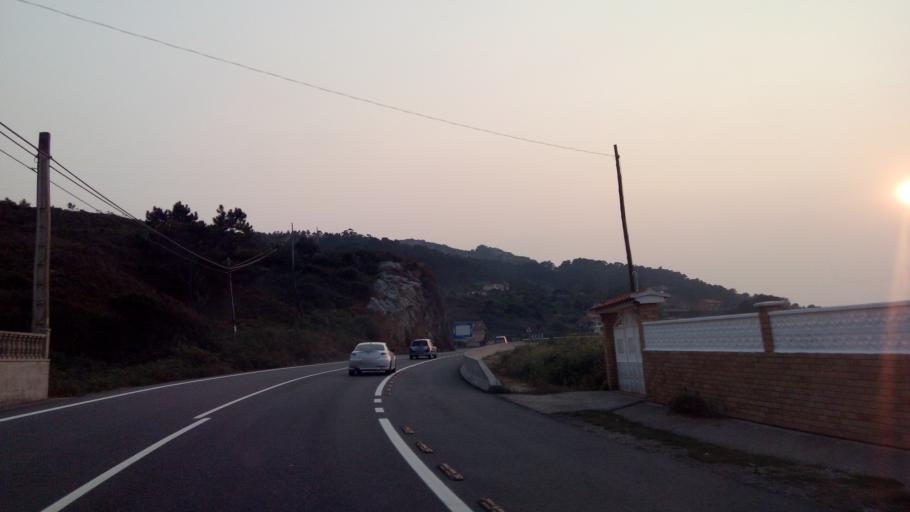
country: ES
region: Galicia
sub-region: Provincia de Pontevedra
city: Baiona
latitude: 42.1111
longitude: -8.8772
